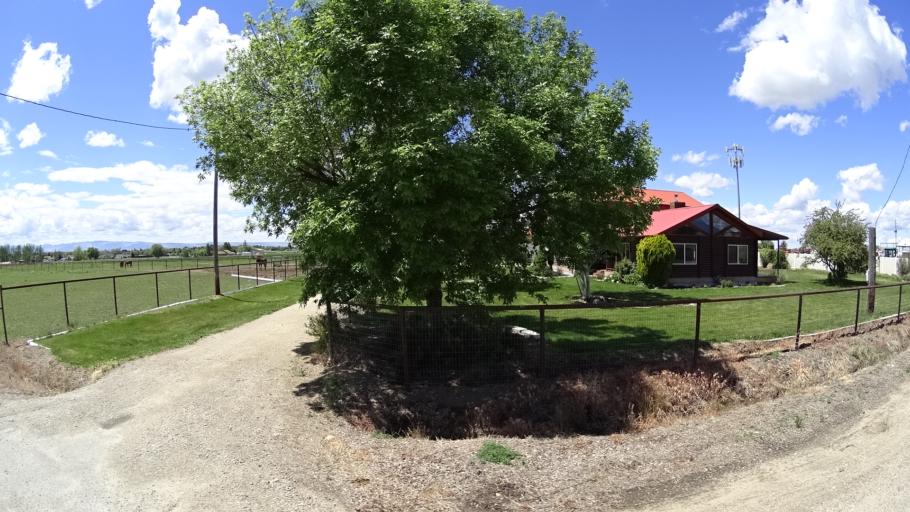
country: US
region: Idaho
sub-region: Ada County
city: Meridian
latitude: 43.5844
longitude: -116.4538
